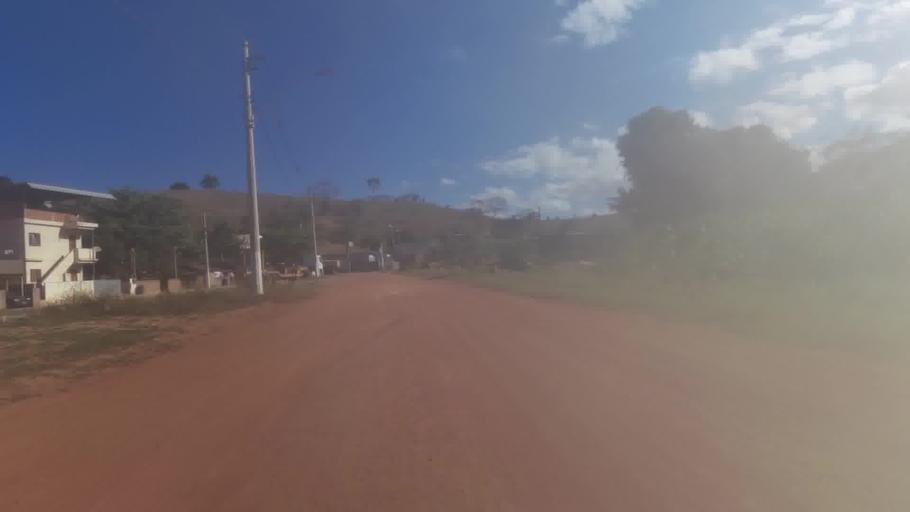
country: BR
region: Espirito Santo
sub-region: Cachoeiro De Itapemirim
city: Cachoeiro de Itapemirim
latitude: -21.0328
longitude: -41.0736
